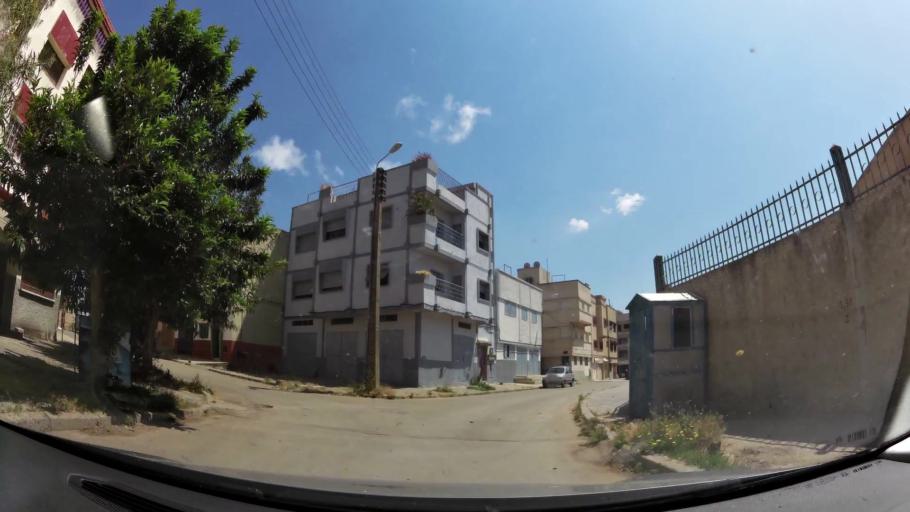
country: MA
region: Rabat-Sale-Zemmour-Zaer
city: Sale
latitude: 34.0452
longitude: -6.7911
